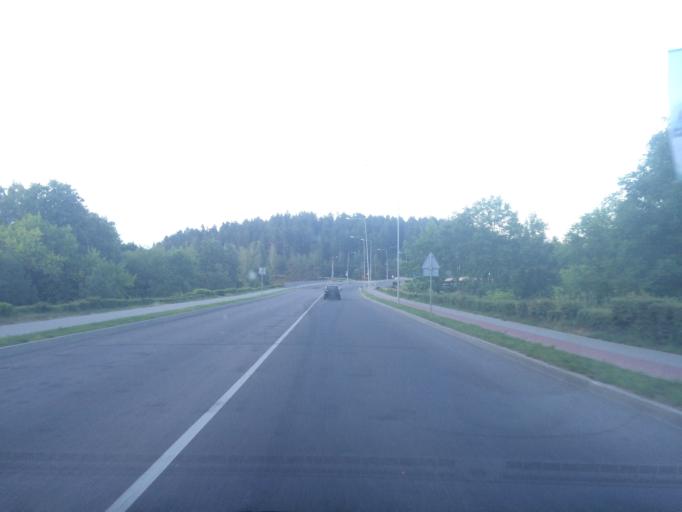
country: LT
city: Zarasai
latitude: 55.7262
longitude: 26.2460
